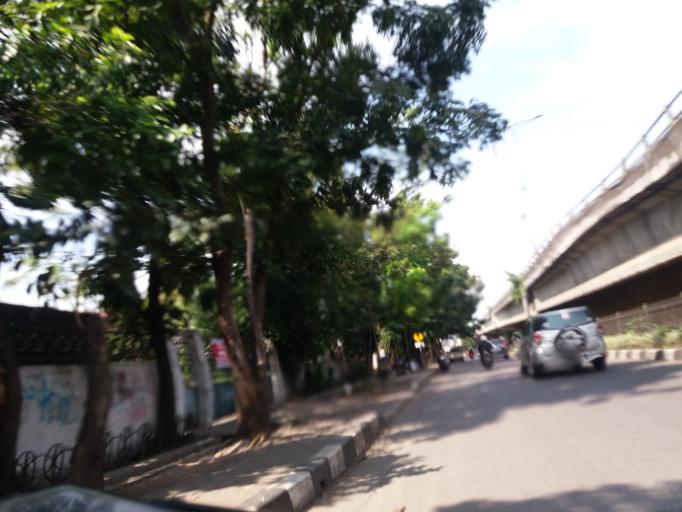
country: ID
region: West Java
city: Bandung
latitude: -6.9209
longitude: 107.6444
